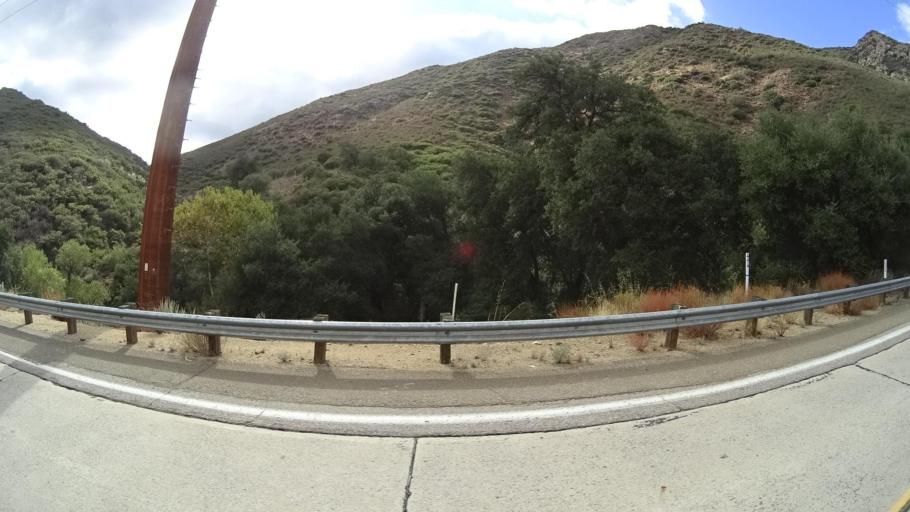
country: US
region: California
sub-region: San Diego County
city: Pine Valley
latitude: 32.7880
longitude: -116.4972
